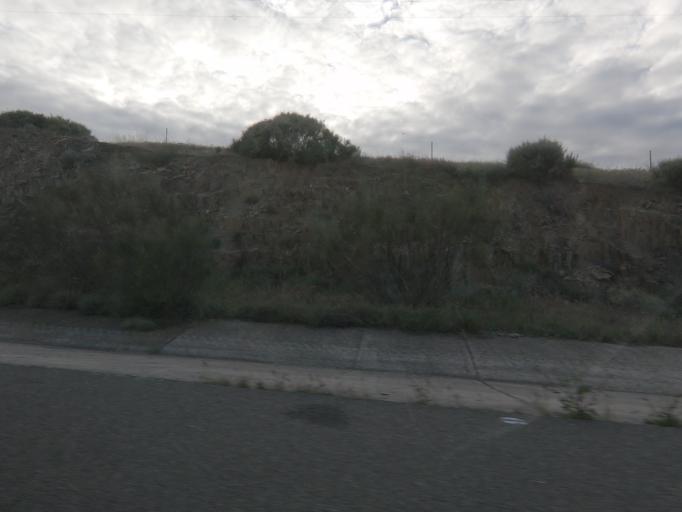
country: ES
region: Extremadura
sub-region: Provincia de Caceres
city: Casar de Caceres
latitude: 39.5954
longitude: -6.4075
